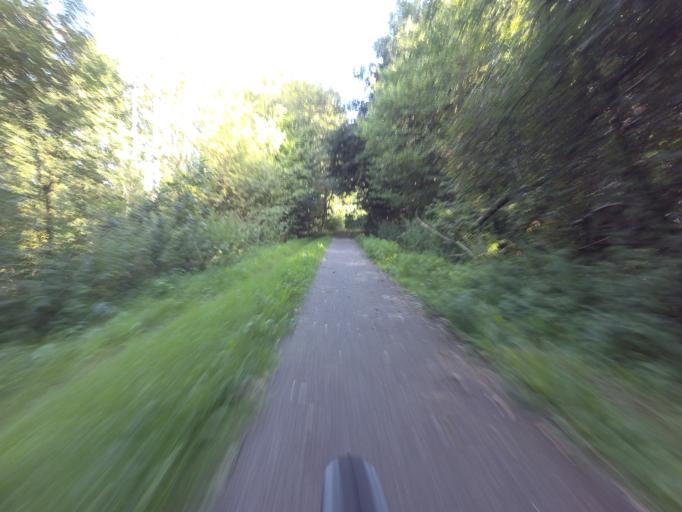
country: DK
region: Central Jutland
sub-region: Horsens Kommune
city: Horsens
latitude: 55.9359
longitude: 9.7743
